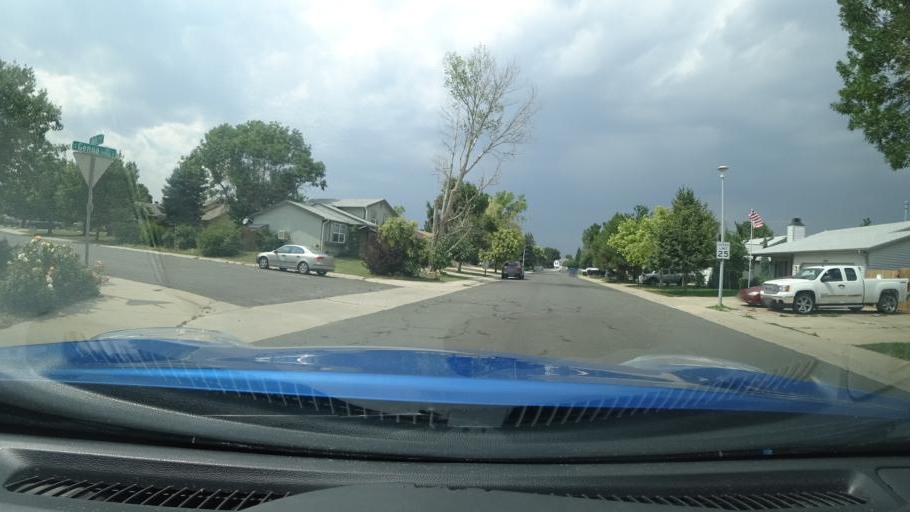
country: US
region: Colorado
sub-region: Adams County
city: Aurora
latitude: 39.6826
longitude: -104.7566
